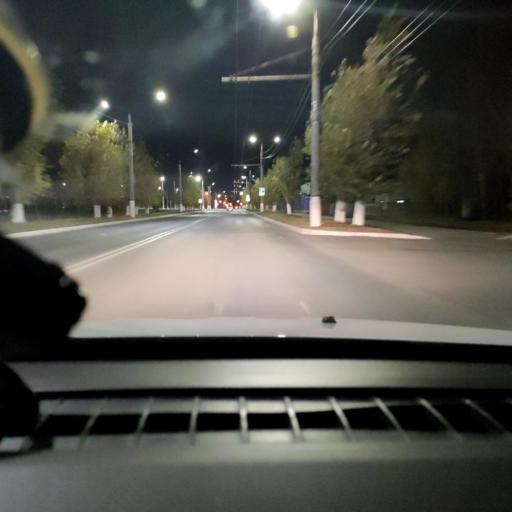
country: RU
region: Samara
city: Novokuybyshevsk
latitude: 53.1015
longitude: 49.9424
